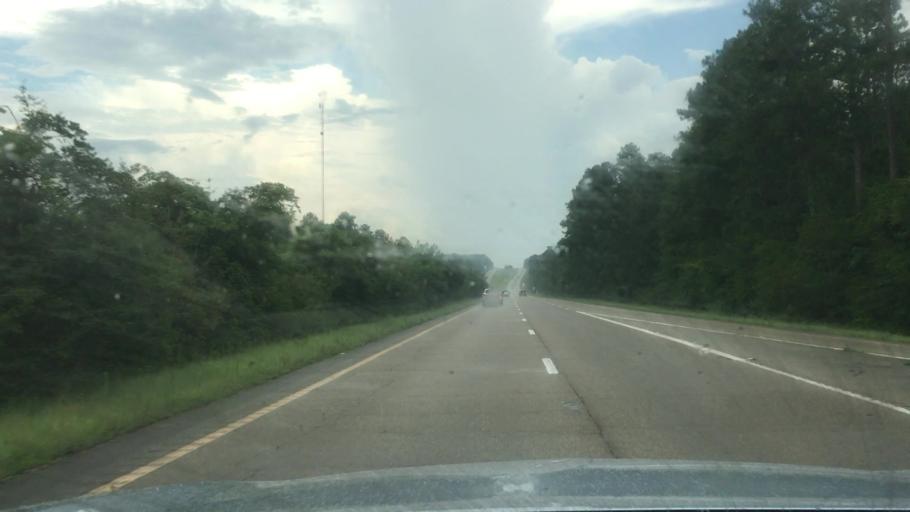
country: US
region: Mississippi
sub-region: Lamar County
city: Purvis
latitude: 31.1430
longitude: -89.3668
